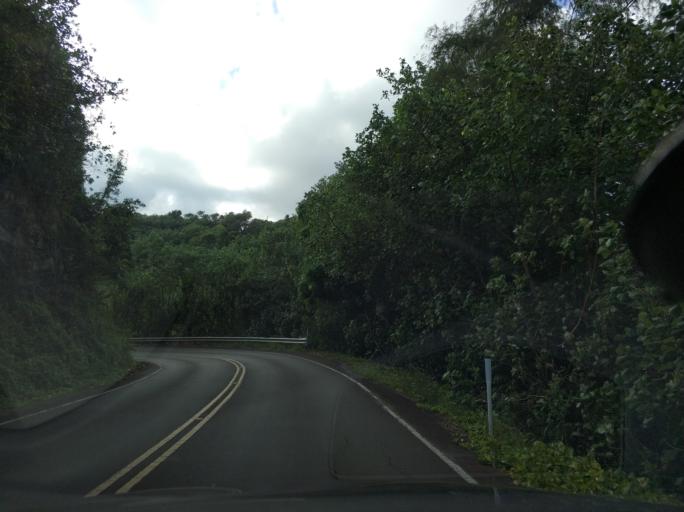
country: US
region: Hawaii
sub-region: Hawaii County
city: Kapaau
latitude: 20.2091
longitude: -155.7385
